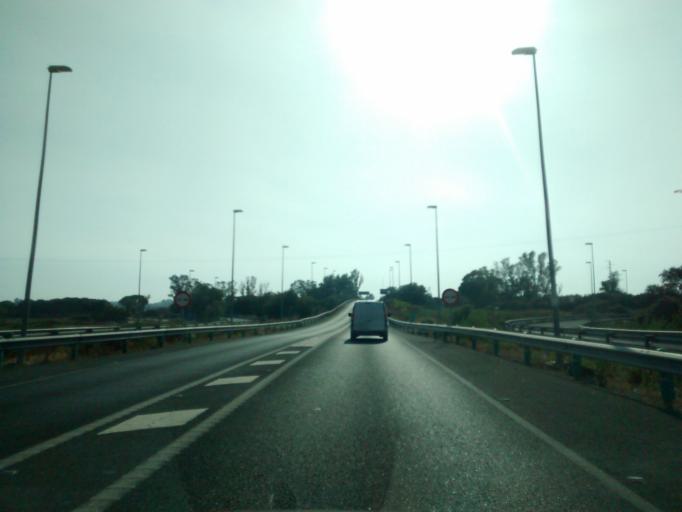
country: ES
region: Andalusia
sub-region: Provincia de Cadiz
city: Jerez de la Frontera
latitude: 36.7047
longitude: -6.0705
